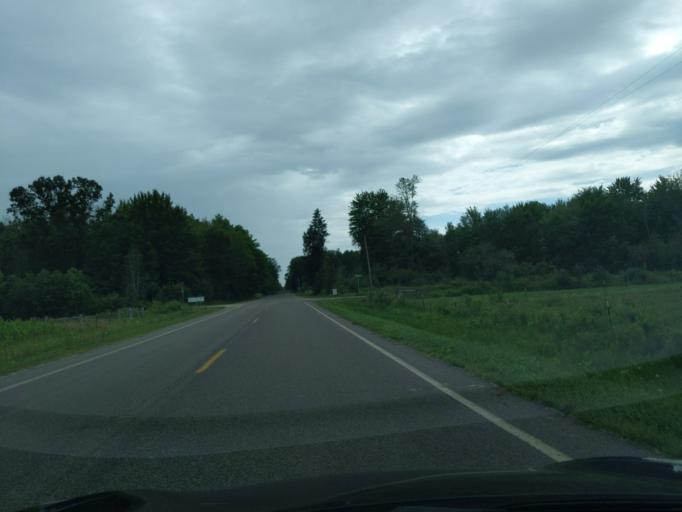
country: US
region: Michigan
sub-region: Clare County
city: Harrison
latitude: 44.0030
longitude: -84.9490
